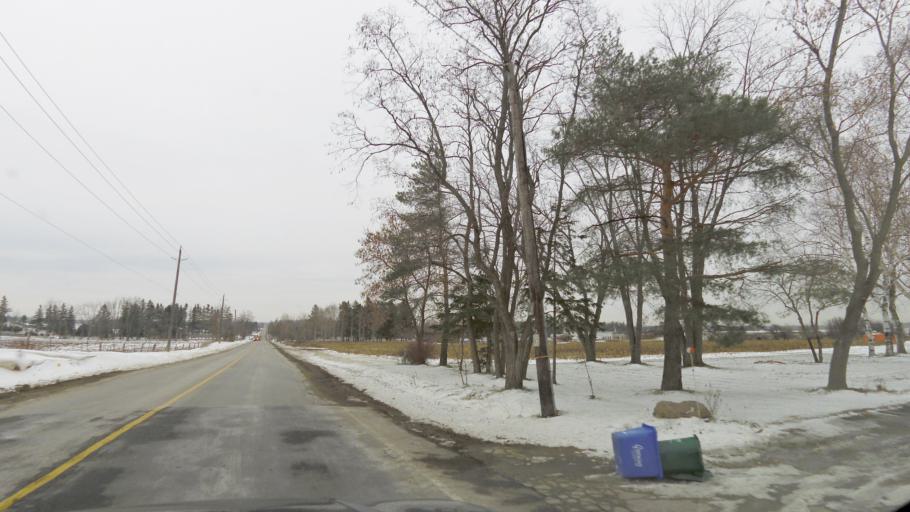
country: CA
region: Ontario
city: Vaughan
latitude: 43.8963
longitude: -79.5903
